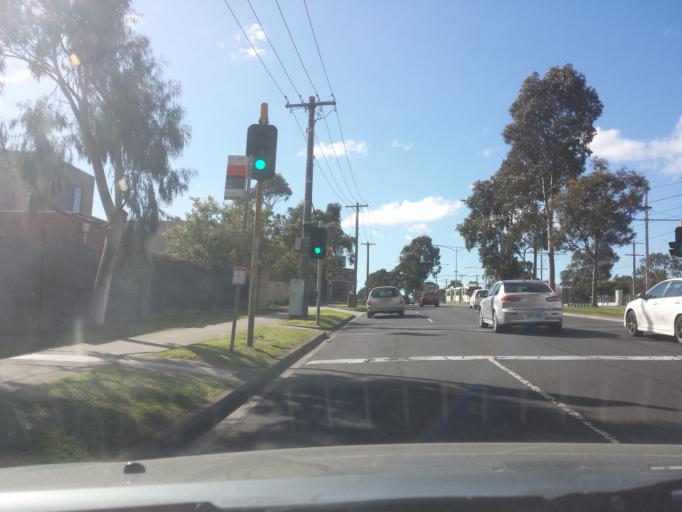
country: AU
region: Victoria
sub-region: Darebin
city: Kingsbury
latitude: -37.7105
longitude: 145.0488
